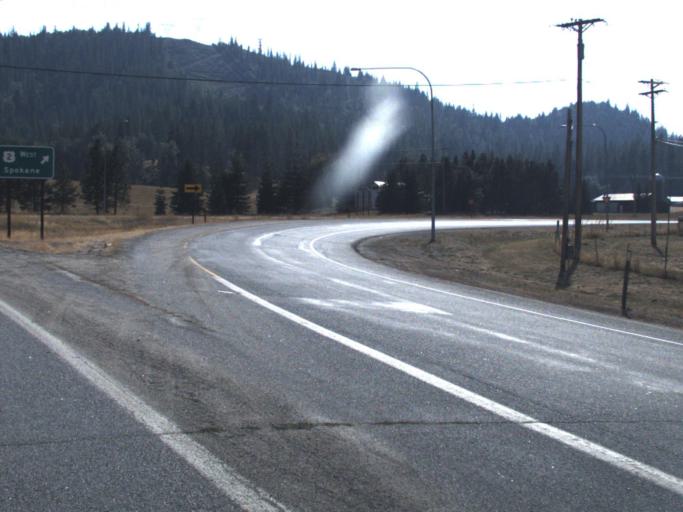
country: US
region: Washington
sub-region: Spokane County
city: Deer Park
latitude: 48.0980
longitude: -117.2786
